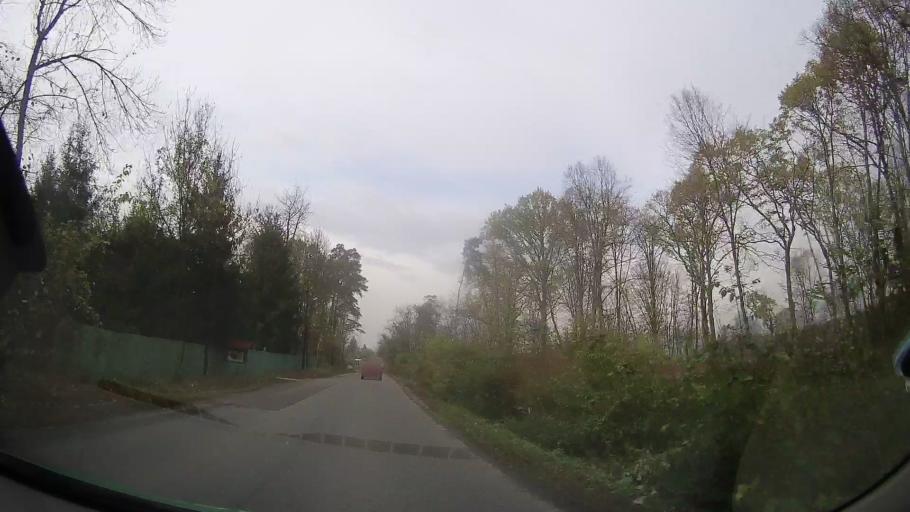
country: RO
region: Prahova
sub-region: Comuna Gorgota
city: Potigrafu
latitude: 44.7701
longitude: 26.1099
